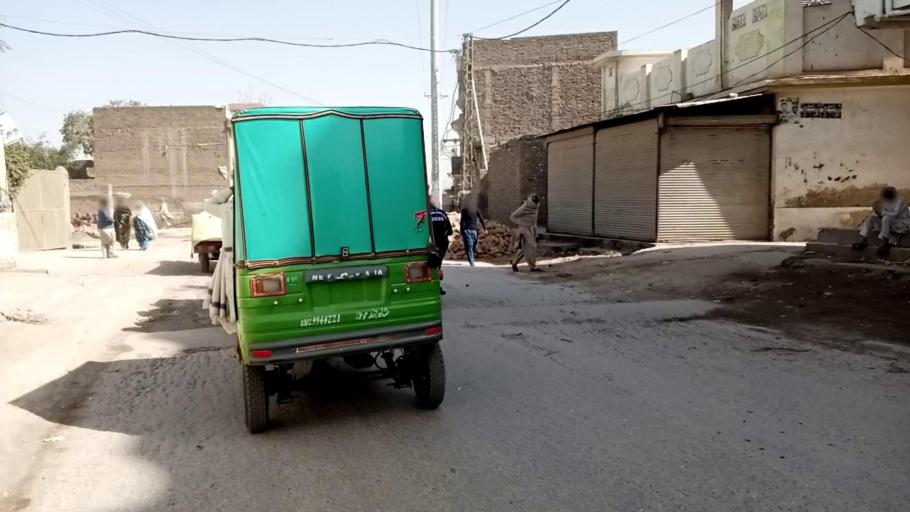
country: PK
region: Khyber Pakhtunkhwa
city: Peshawar
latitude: 34.0063
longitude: 71.6412
